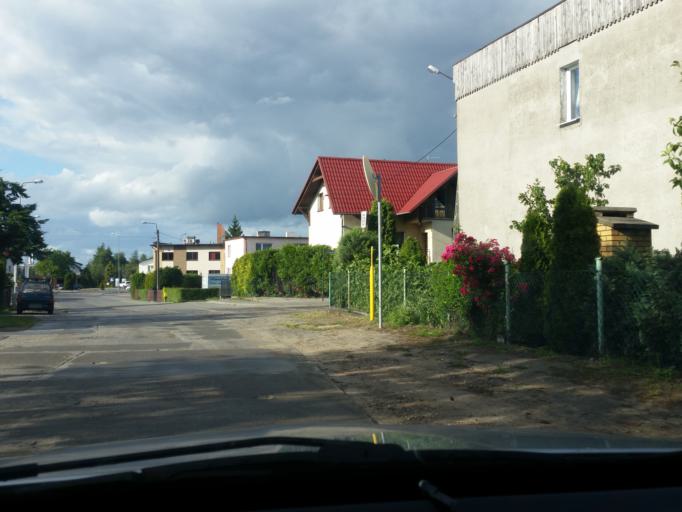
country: PL
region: Pomeranian Voivodeship
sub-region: Powiat chojnicki
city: Chojnice
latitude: 53.7041
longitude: 17.5455
